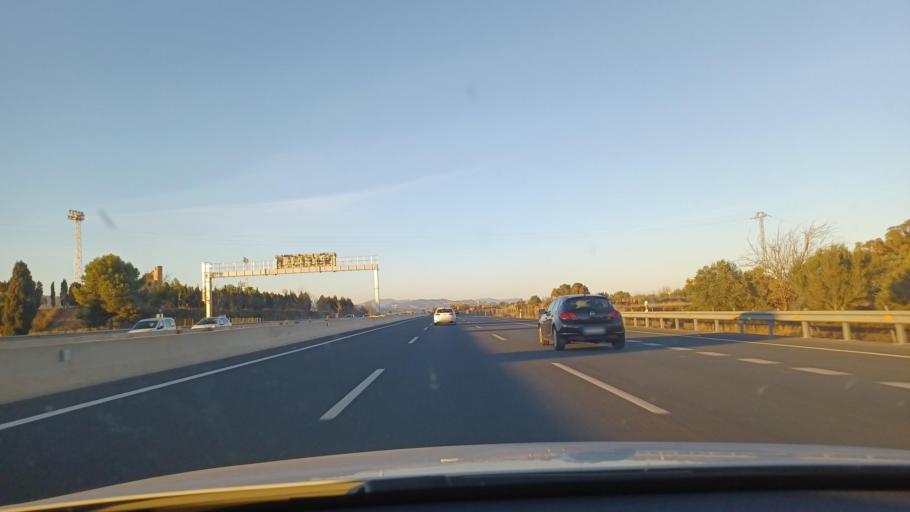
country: ES
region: Valencia
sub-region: Provincia de Valencia
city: Puig
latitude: 39.5902
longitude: -0.2933
